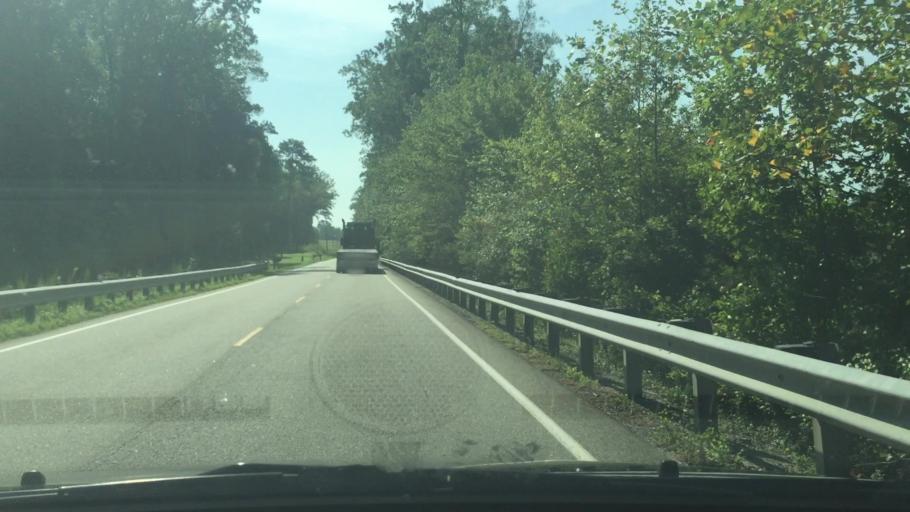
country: US
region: Virginia
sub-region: Prince George County
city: Prince George
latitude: 37.0702
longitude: -77.3413
